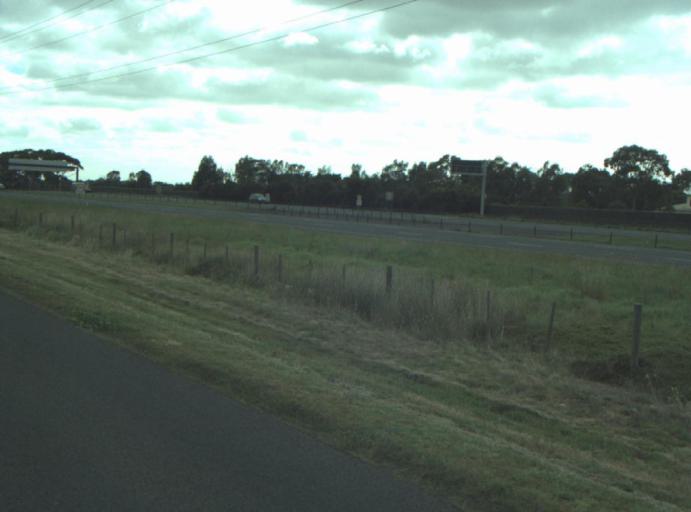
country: AU
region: Victoria
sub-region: Greater Geelong
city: Lara
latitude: -38.0476
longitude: 144.4018
